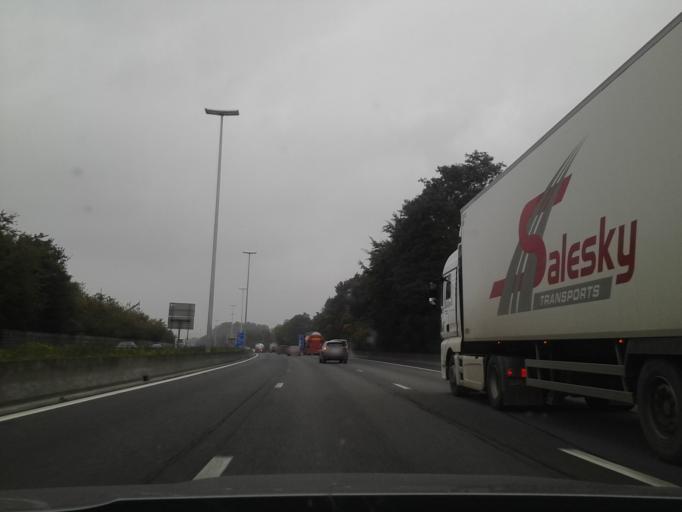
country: BE
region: Wallonia
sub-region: Province du Hainaut
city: Mons
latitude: 50.4776
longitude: 3.9383
